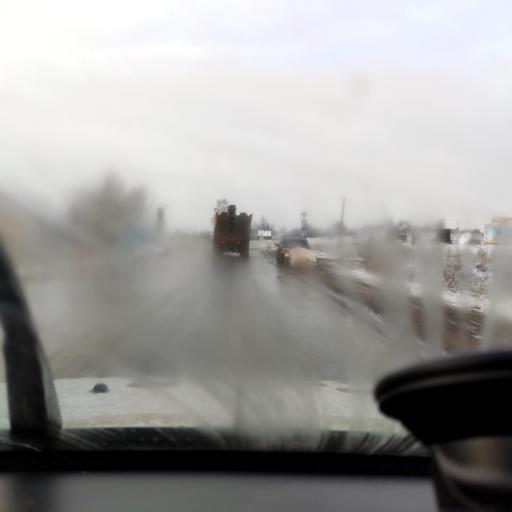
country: RU
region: Perm
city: Nytva
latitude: 57.9503
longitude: 55.3557
